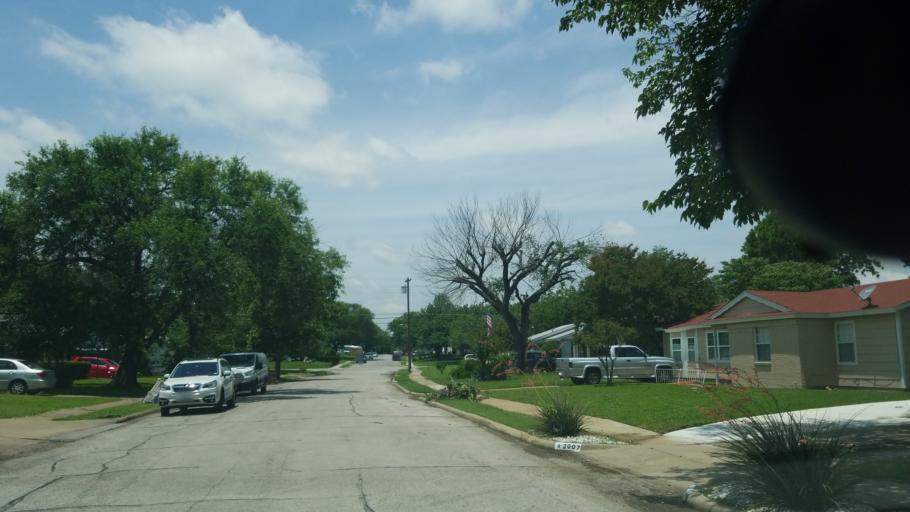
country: US
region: Texas
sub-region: Dallas County
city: Irving
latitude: 32.8479
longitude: -96.9714
